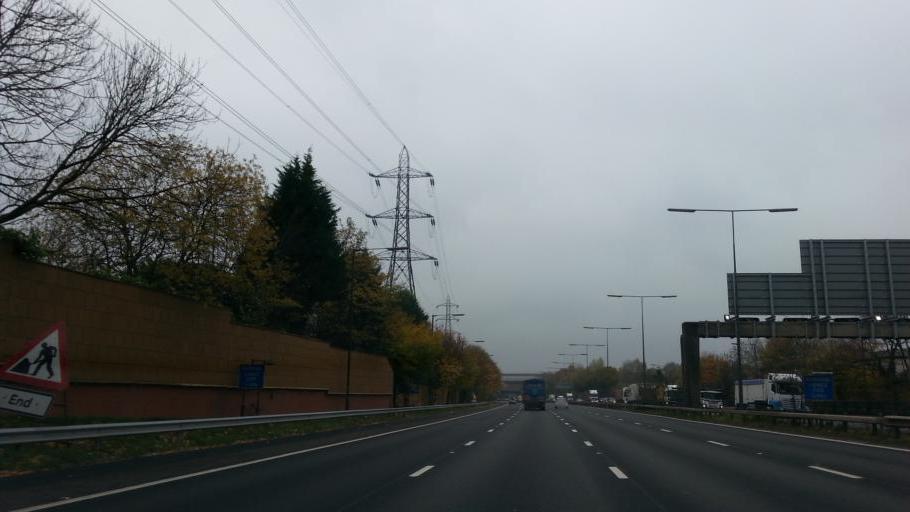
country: GB
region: England
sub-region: Borough of Bury
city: Prestwich
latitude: 53.5438
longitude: -2.2787
